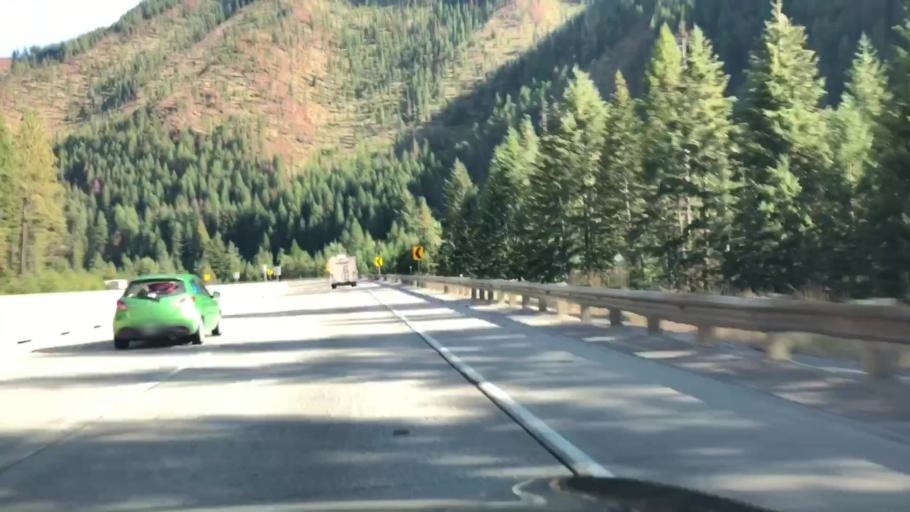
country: US
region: Montana
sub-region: Sanders County
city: Thompson Falls
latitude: 47.3032
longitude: -115.2019
